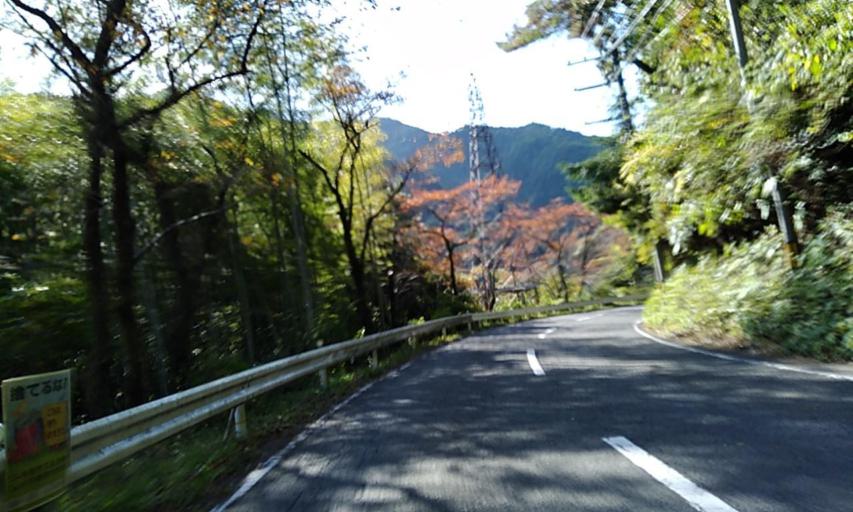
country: JP
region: Wakayama
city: Iwade
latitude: 34.0899
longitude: 135.3654
